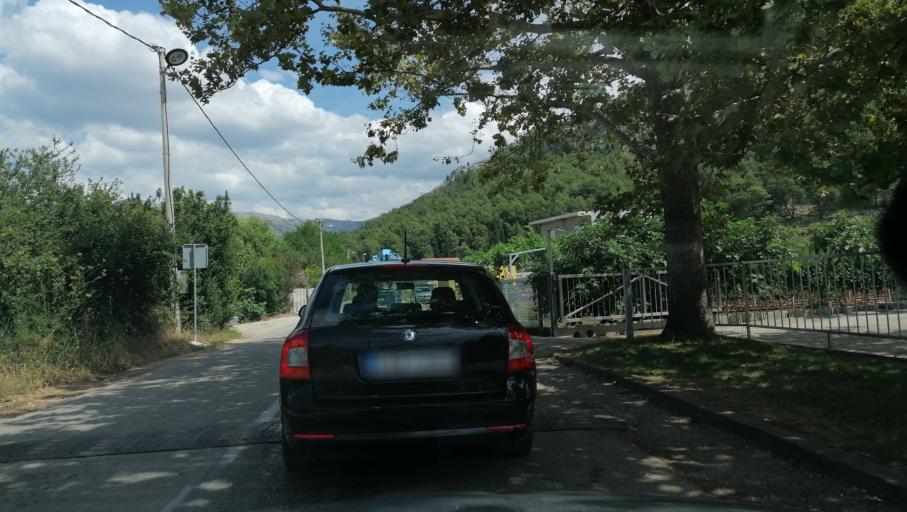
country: BA
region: Republika Srpska
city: Trebinje
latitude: 42.6831
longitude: 18.3348
